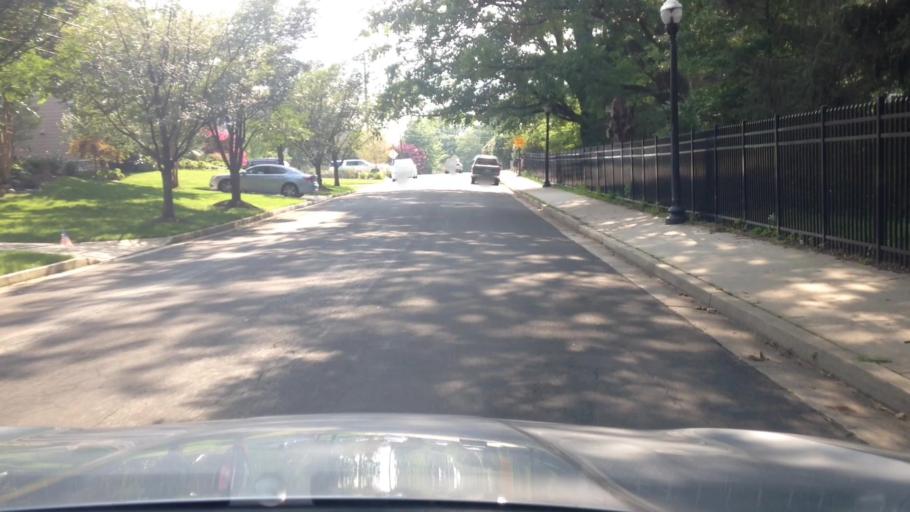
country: US
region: Virginia
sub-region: Fairfax County
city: Seven Corners
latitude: 38.8996
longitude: -77.1403
